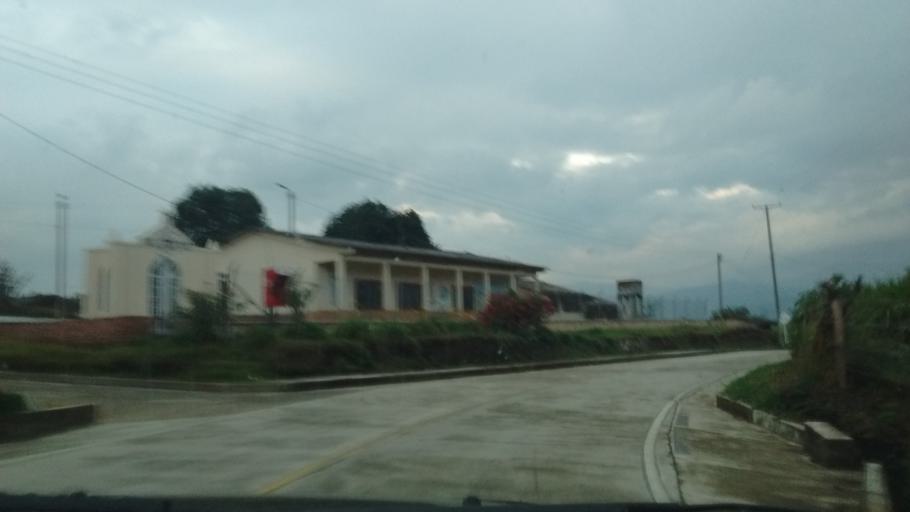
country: CO
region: Cauca
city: Lopez
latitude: 2.3799
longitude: -76.7185
